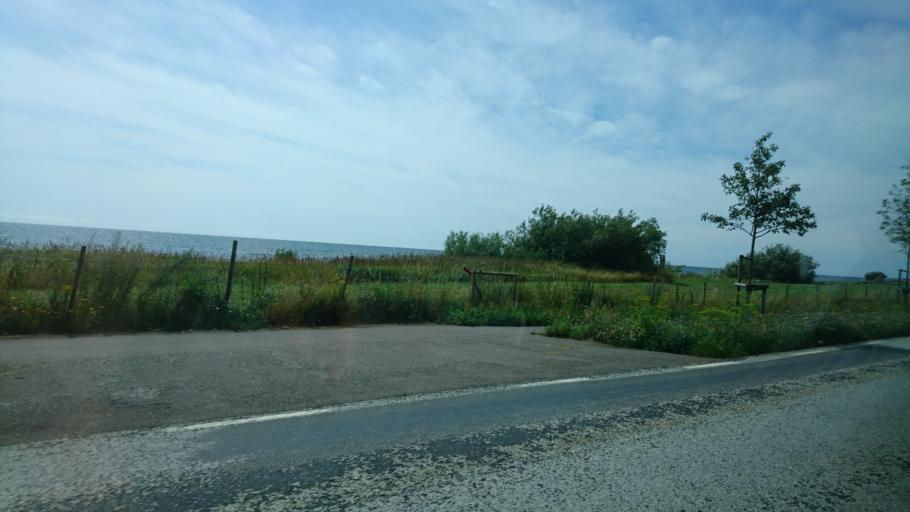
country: SE
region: Skane
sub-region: Skurups Kommun
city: Skivarp
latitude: 55.3879
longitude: 13.5334
